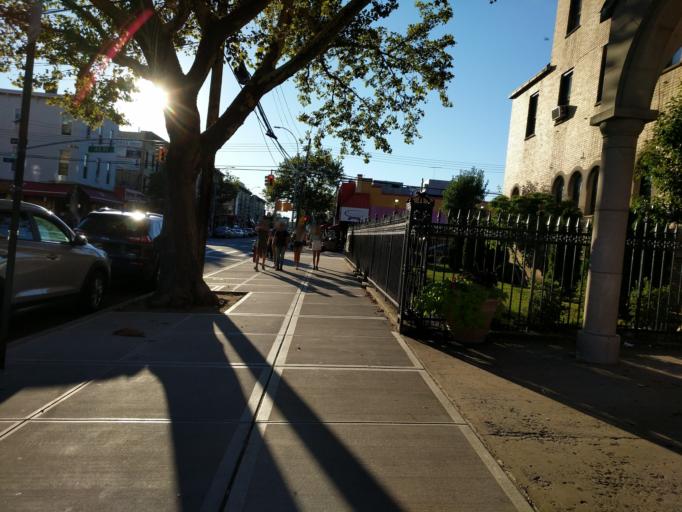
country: US
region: New York
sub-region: Queens County
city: Long Island City
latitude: 40.7626
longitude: -73.9121
